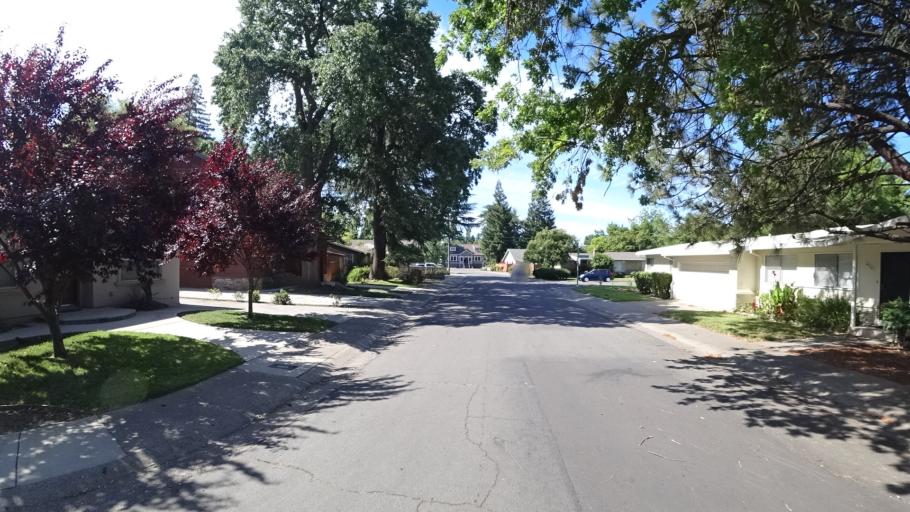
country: US
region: California
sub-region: Sacramento County
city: Sacramento
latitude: 38.5325
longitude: -121.4995
